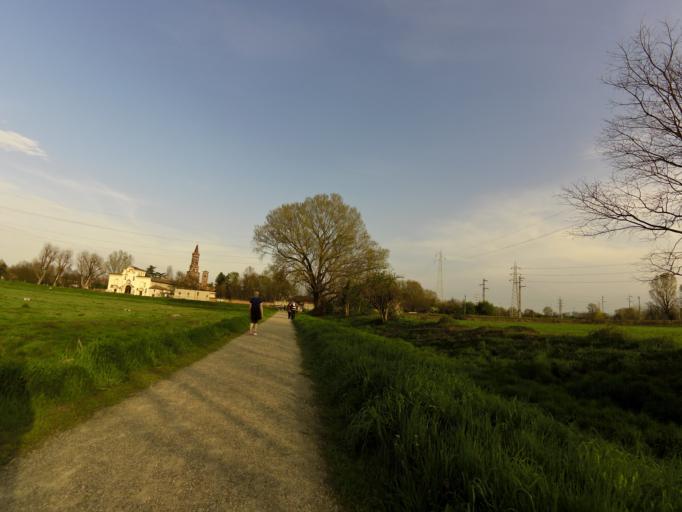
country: IT
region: Lombardy
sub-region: Citta metropolitana di Milano
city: Chiaravalle
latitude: 45.4167
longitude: 9.2331
